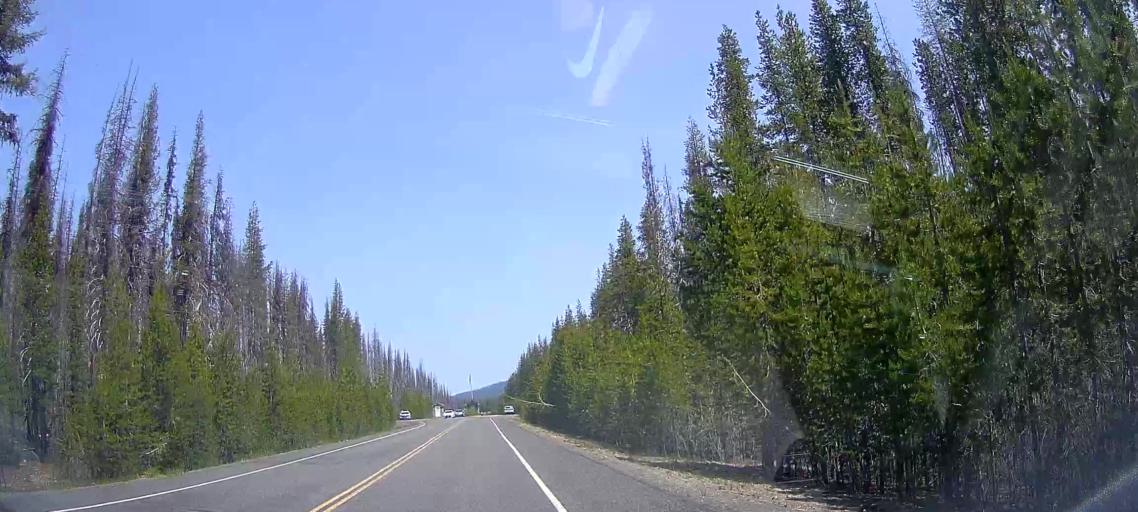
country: US
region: Oregon
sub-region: Lane County
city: Oakridge
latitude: 43.0765
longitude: -122.1181
